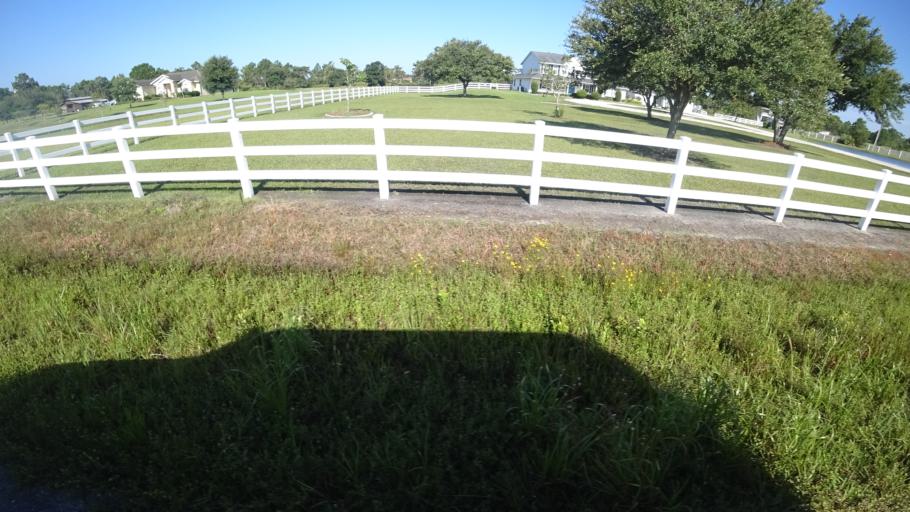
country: US
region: Florida
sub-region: Sarasota County
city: The Meadows
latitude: 27.4112
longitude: -82.3121
